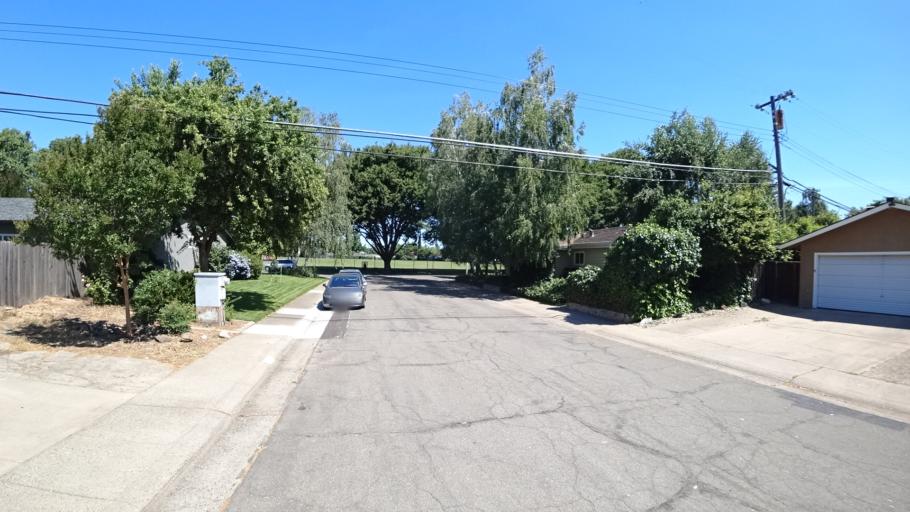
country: US
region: California
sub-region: Sacramento County
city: Rosemont
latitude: 38.5530
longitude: -121.3980
